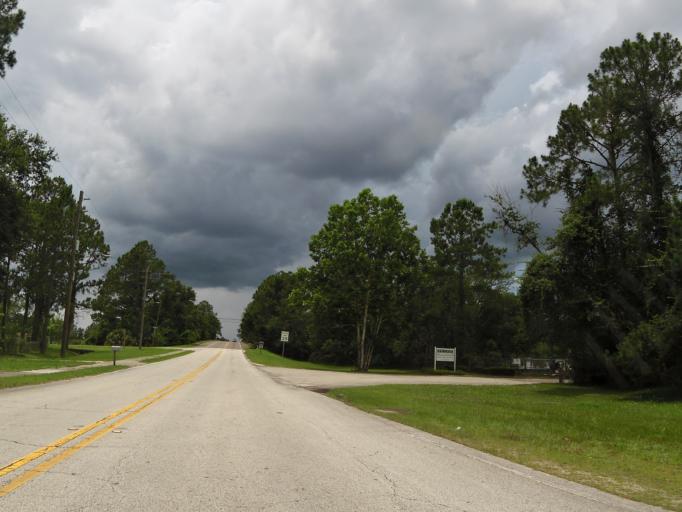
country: US
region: Florida
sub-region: Duval County
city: Jacksonville
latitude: 30.4141
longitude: -81.6544
